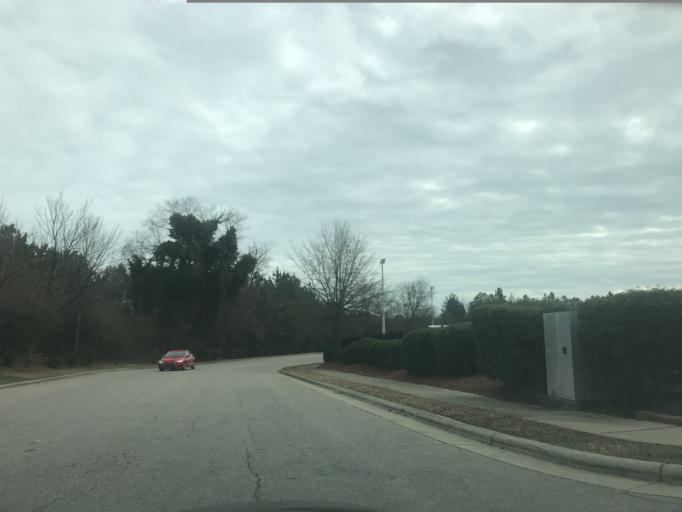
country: US
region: North Carolina
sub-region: Wake County
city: West Raleigh
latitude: 35.8838
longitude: -78.5917
